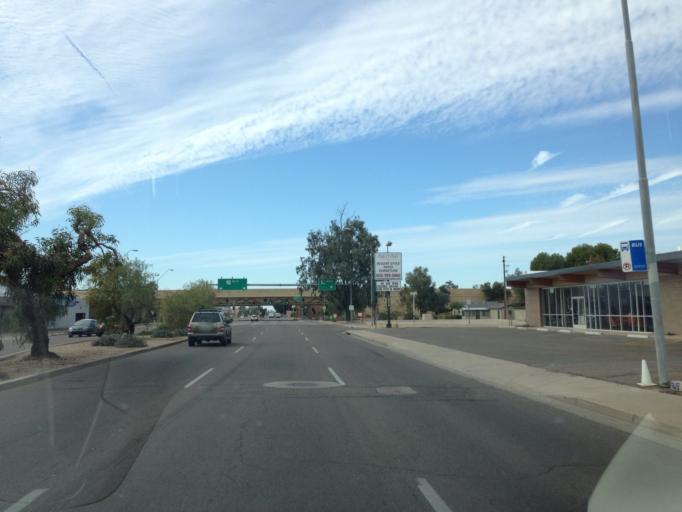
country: US
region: Arizona
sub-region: Maricopa County
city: Phoenix
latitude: 33.4948
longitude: -112.0413
